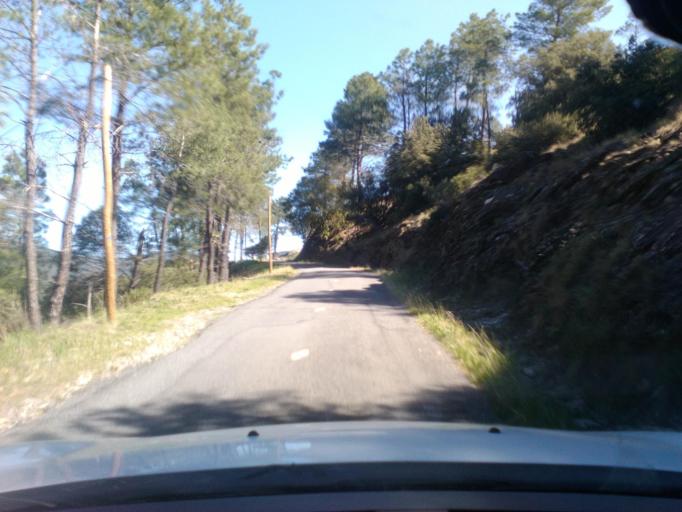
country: FR
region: Languedoc-Roussillon
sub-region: Departement du Gard
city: Valleraugue
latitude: 44.1707
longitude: 3.7513
